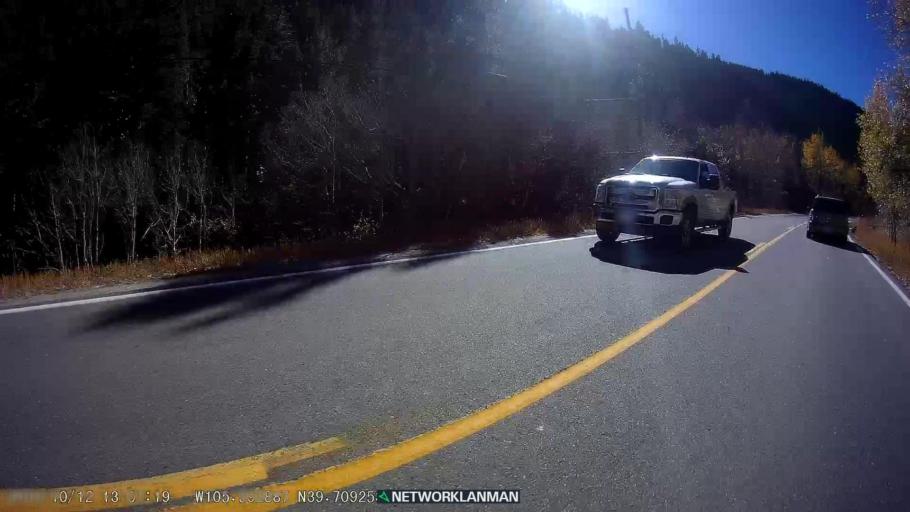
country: US
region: Colorado
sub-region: Clear Creek County
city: Idaho Springs
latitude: 39.7091
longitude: -105.5931
